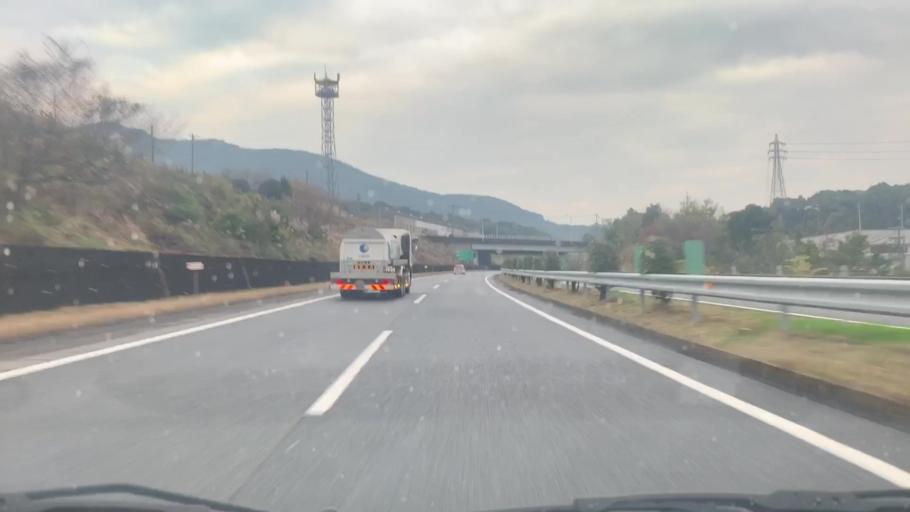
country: JP
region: Nagasaki
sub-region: Isahaya-shi
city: Isahaya
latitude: 32.8232
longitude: 130.0037
